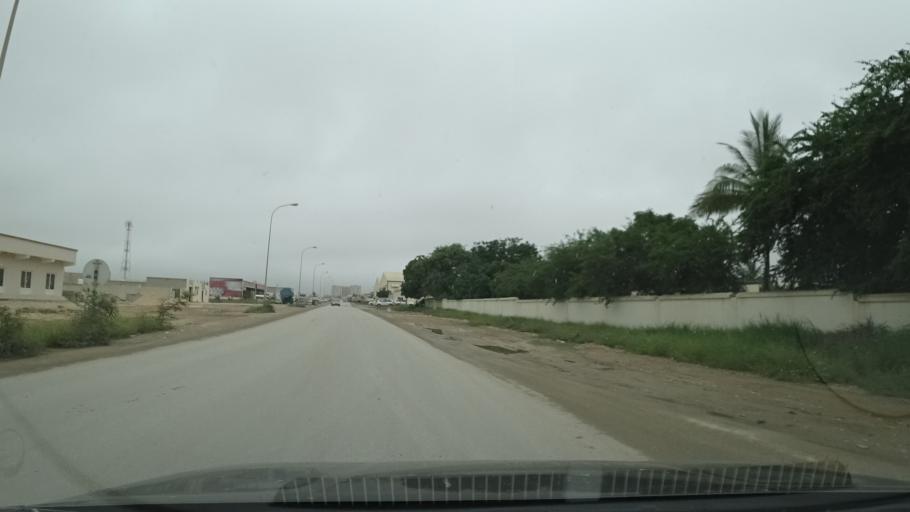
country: OM
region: Zufar
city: Salalah
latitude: 17.0130
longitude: 54.0444
